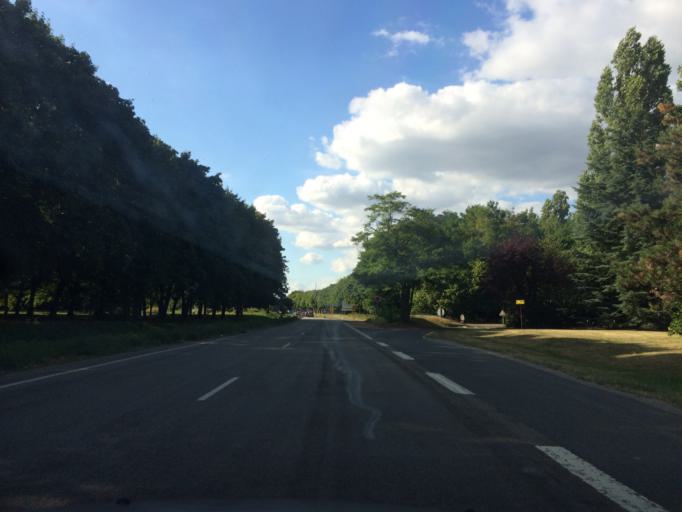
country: FR
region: Ile-de-France
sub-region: Departement de l'Essonne
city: Lisses
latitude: 48.6154
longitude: 2.4235
